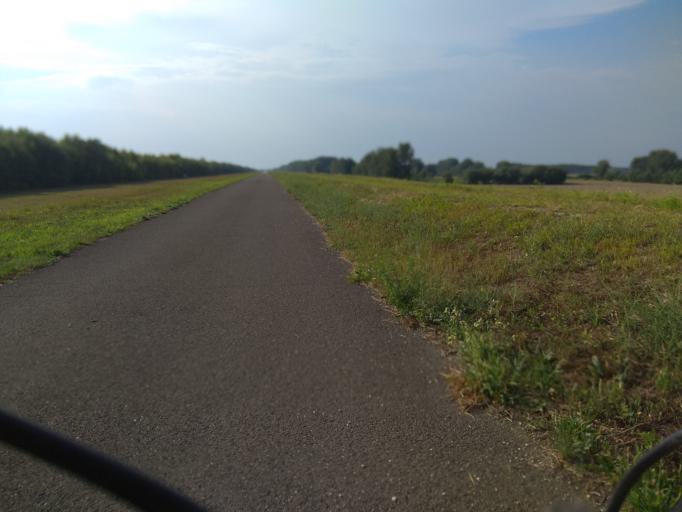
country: SK
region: Trnavsky
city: Gabcikovo
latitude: 47.8380
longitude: 17.5920
